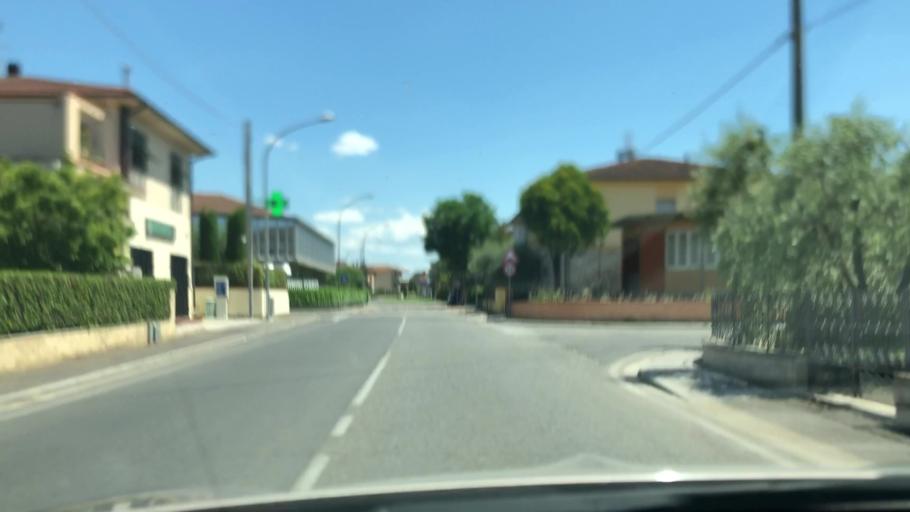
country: IT
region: Tuscany
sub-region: Province of Pisa
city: Ponsacco
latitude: 43.6171
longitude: 10.6385
